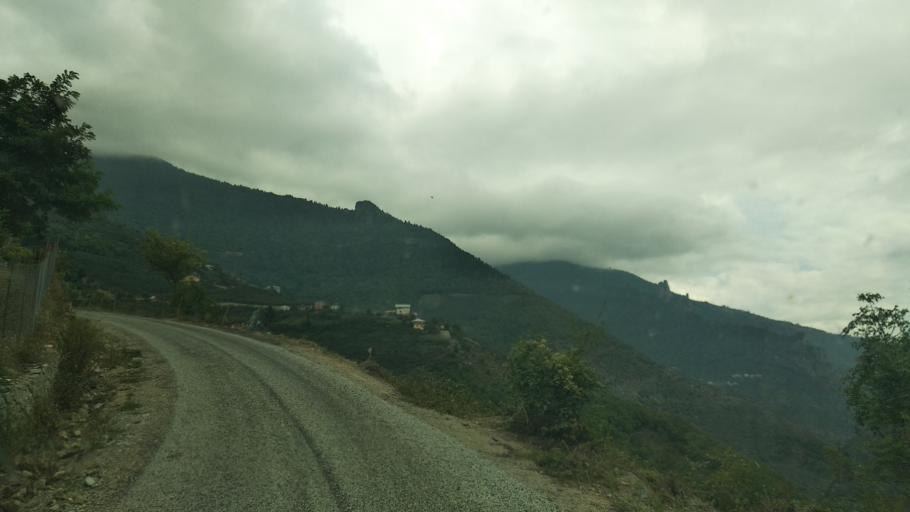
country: TR
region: Giresun
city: Dogankent
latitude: 40.7411
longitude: 38.9896
